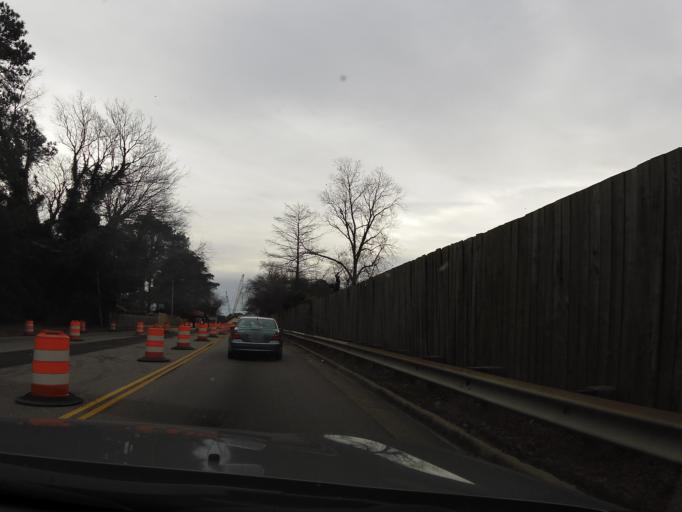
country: US
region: Virginia
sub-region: City of Portsmouth
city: Portsmouth Heights
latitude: 36.8450
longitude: -76.3683
